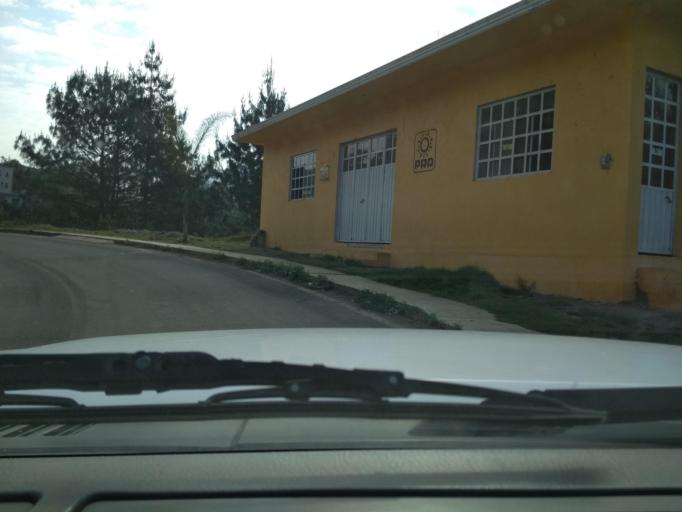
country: MX
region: Veracruz
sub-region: Soledad Atzompa
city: Tlatilpa
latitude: 18.7484
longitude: -97.1559
